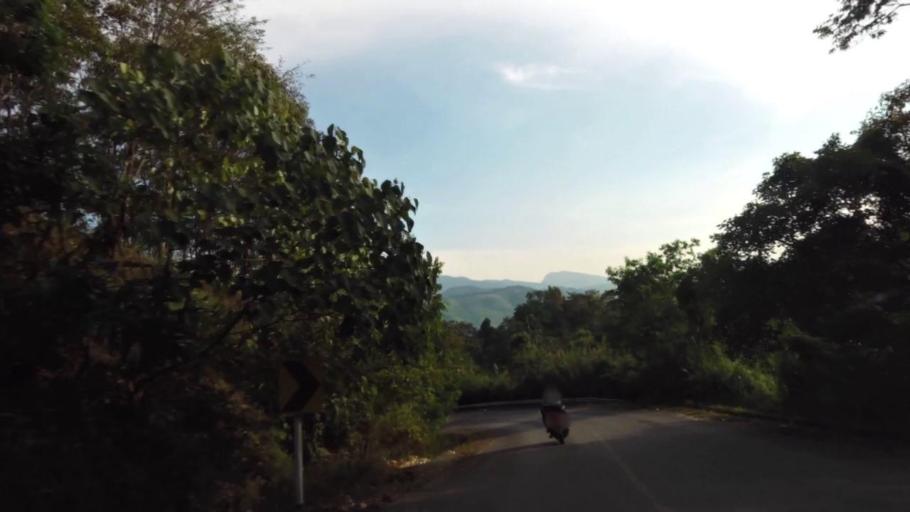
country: TH
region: Chiang Rai
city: Khun Tan
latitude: 19.8530
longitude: 100.3789
